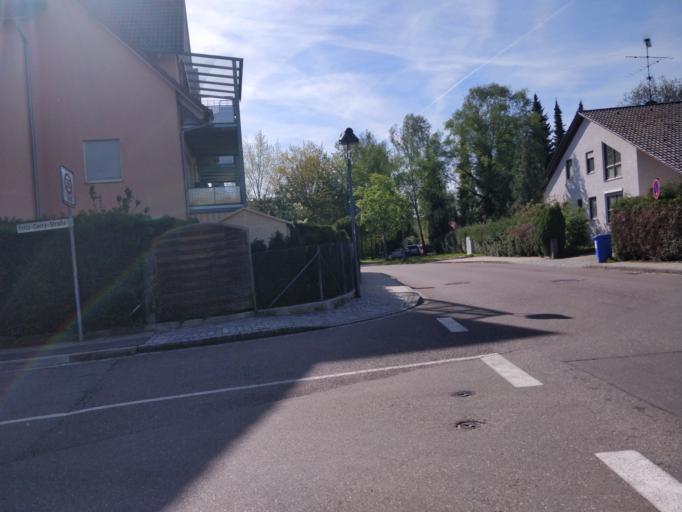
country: DE
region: Bavaria
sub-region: Swabia
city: Wertingen
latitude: 48.5628
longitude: 10.6840
